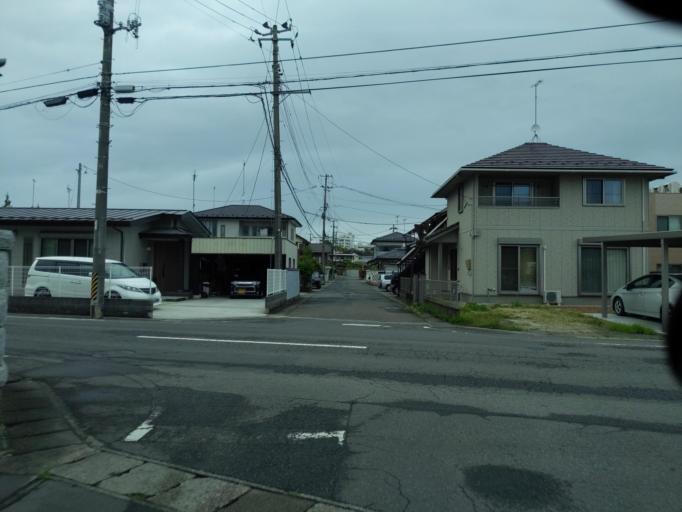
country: JP
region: Fukushima
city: Koriyama
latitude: 37.3575
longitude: 140.3592
